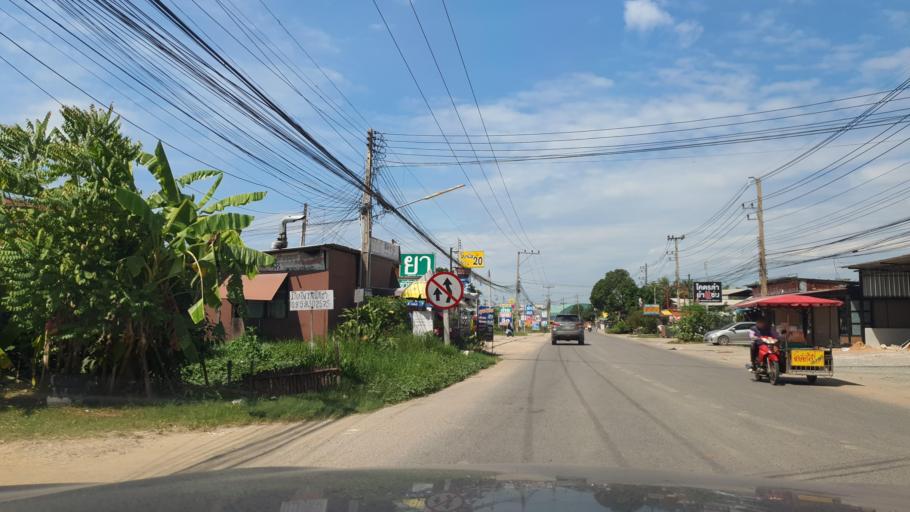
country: TH
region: Chon Buri
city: Phatthaya
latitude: 12.9601
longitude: 100.9233
